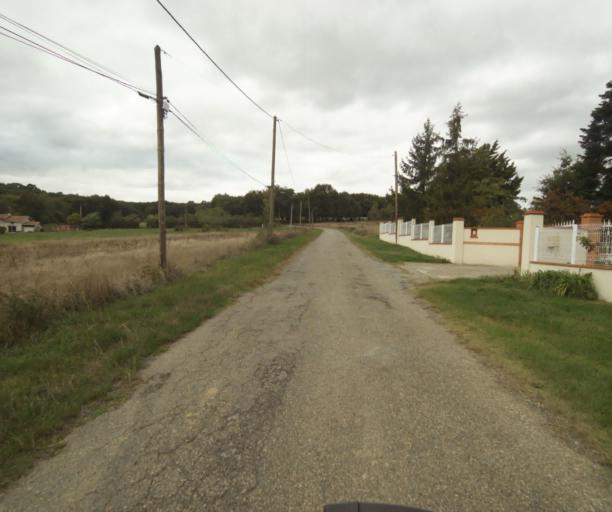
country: FR
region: Midi-Pyrenees
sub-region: Departement du Tarn-et-Garonne
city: Beaumont-de-Lomagne
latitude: 43.8423
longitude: 1.1031
